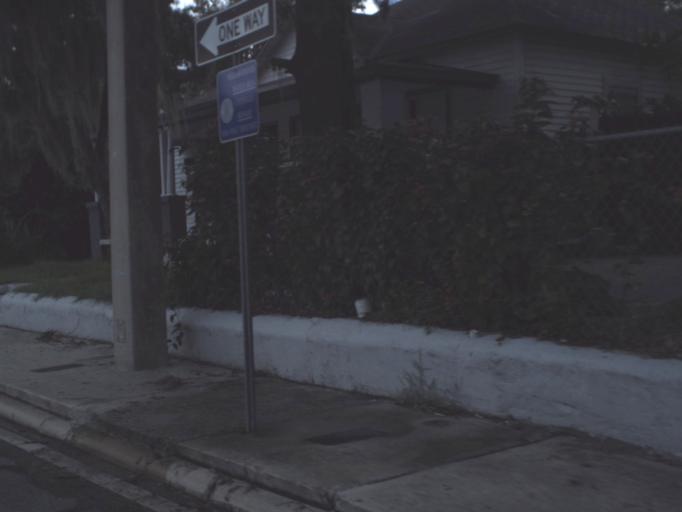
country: US
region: Florida
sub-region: Hillsborough County
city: Tampa
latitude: 27.9710
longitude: -82.4609
